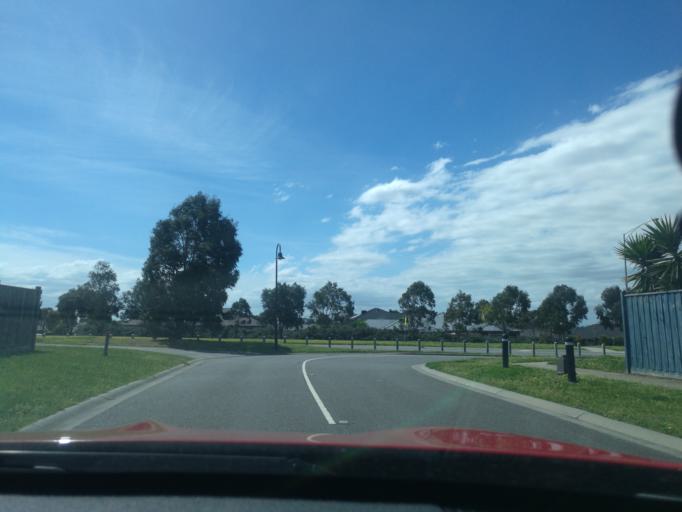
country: AU
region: Victoria
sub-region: Casey
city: Lynbrook
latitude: -38.0640
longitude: 145.2461
